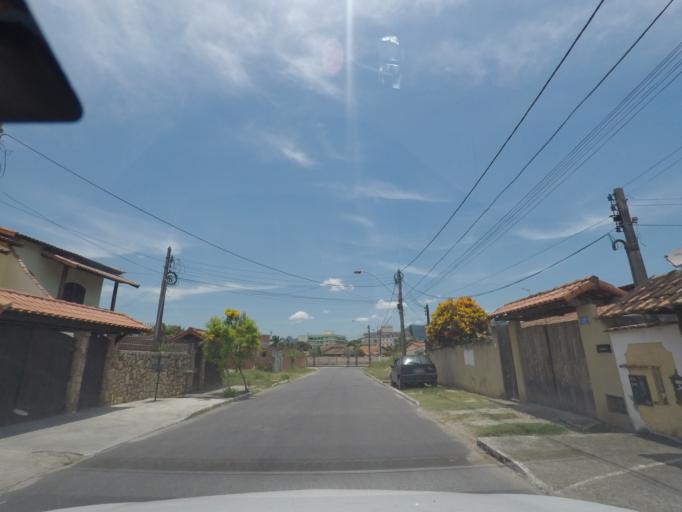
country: BR
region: Rio de Janeiro
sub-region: Marica
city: Marica
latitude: -22.9229
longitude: -42.8215
